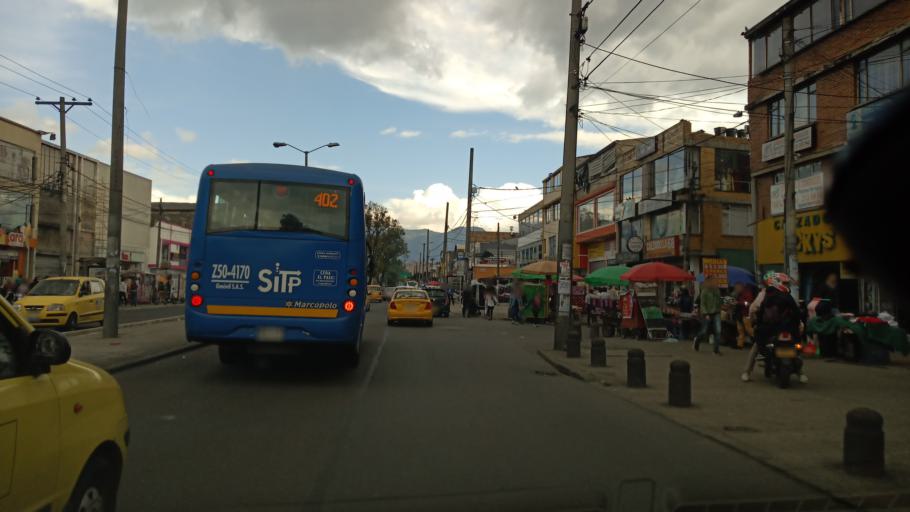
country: CO
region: Bogota D.C.
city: Barrio San Luis
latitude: 4.6824
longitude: -74.0902
